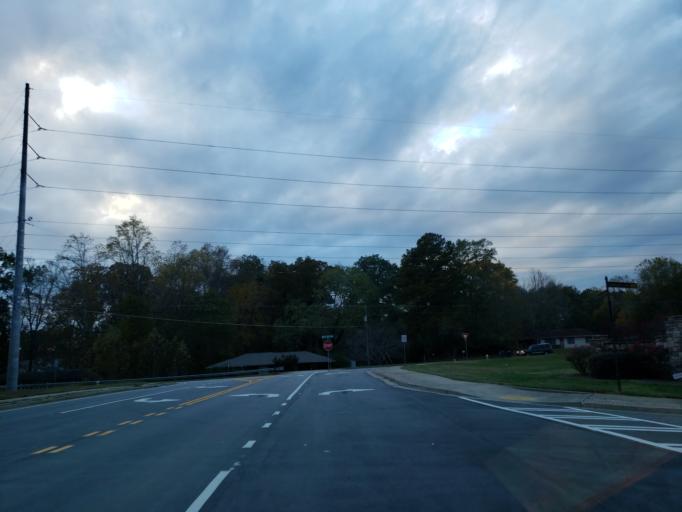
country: US
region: Georgia
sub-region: Cobb County
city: Acworth
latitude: 34.0344
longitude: -84.6914
